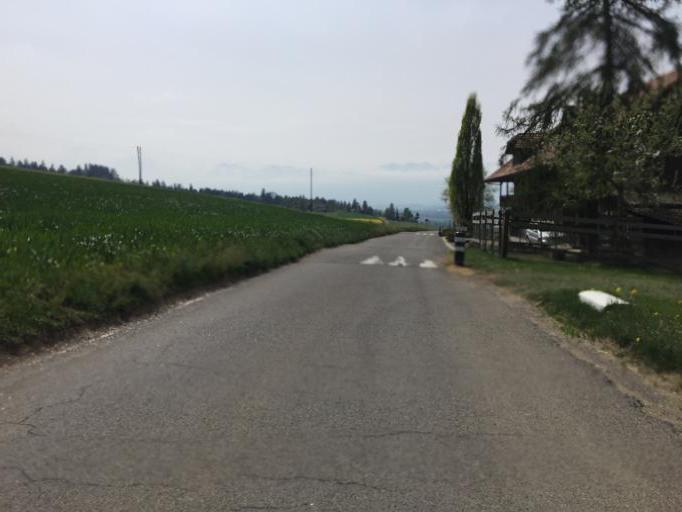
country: CH
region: Bern
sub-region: Bern-Mittelland District
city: Niederwichtrach
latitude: 46.8623
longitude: 7.5818
